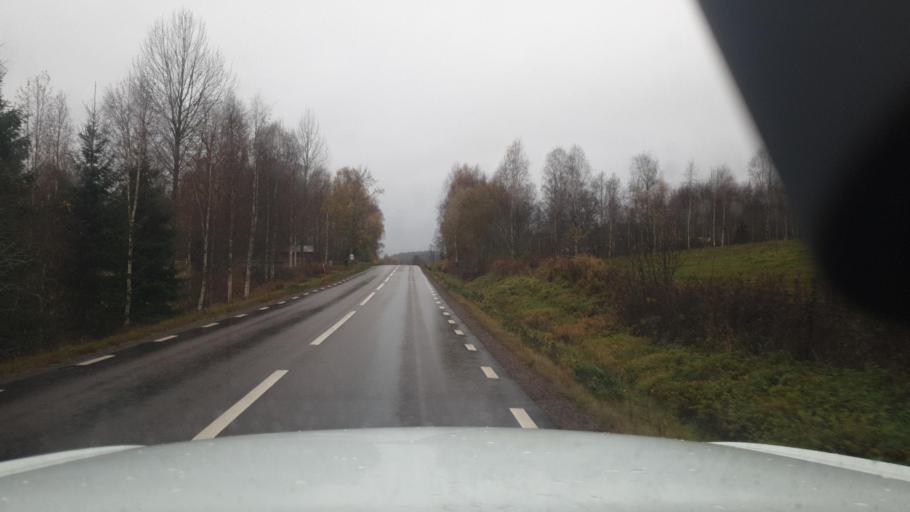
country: SE
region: Vaermland
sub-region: Torsby Kommun
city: Torsby
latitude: 59.9354
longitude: 12.9004
